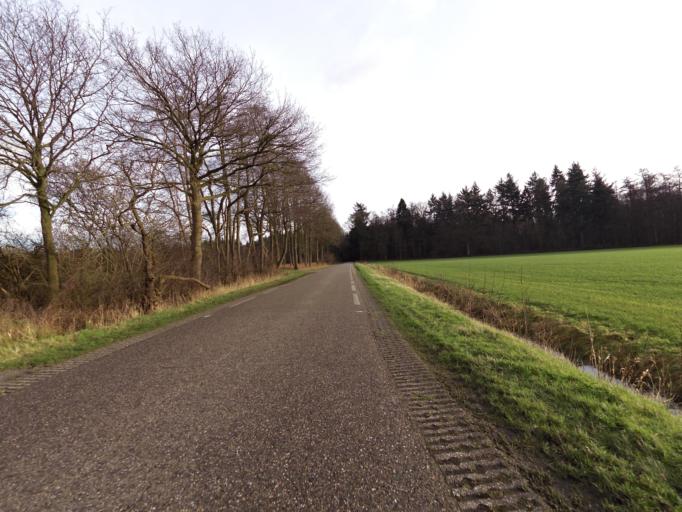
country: NL
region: Gelderland
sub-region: Gemeente Bronckhorst
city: Zelhem
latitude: 51.9694
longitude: 6.3653
